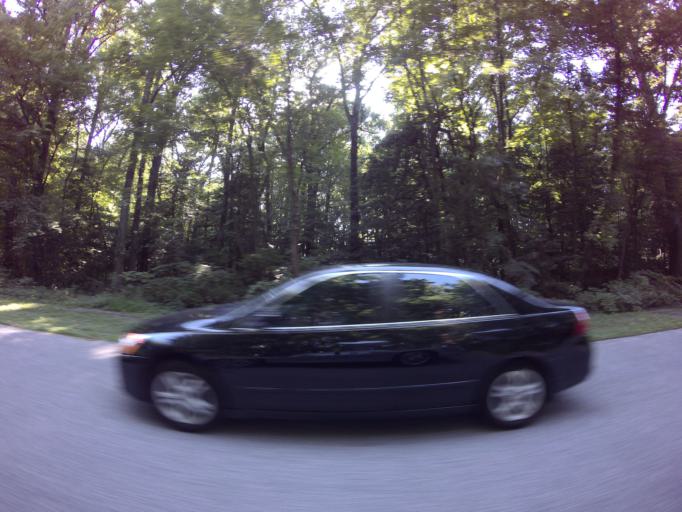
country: US
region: Maryland
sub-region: Baltimore County
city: Edgemere
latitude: 39.2246
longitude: -76.4288
